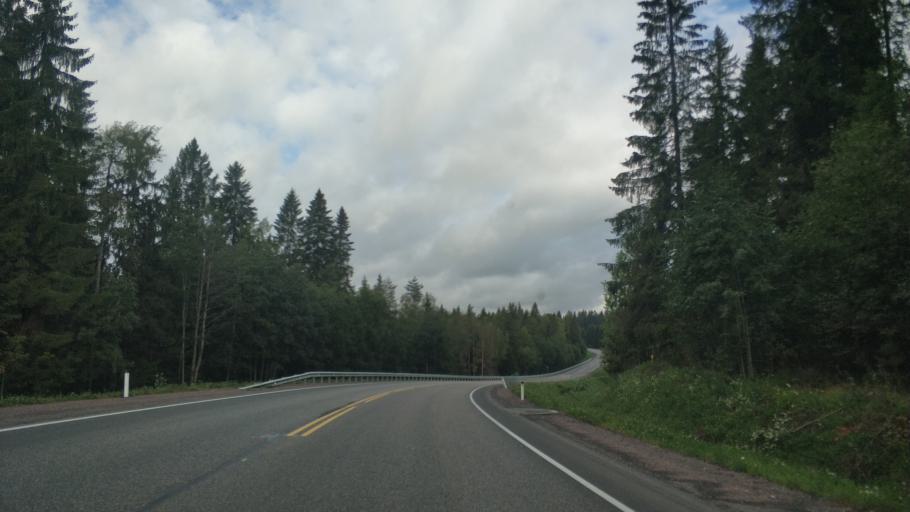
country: RU
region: Republic of Karelia
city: Khelyulya
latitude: 61.7878
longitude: 30.6344
